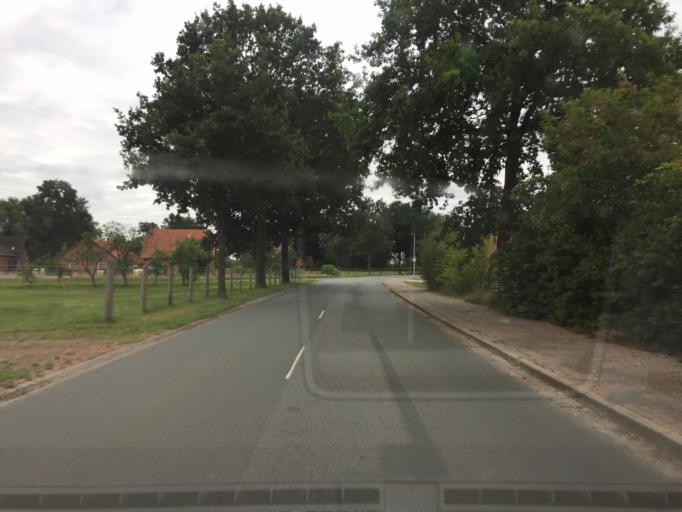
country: DE
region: Lower Saxony
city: Ehrenburg
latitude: 52.7521
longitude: 8.7145
